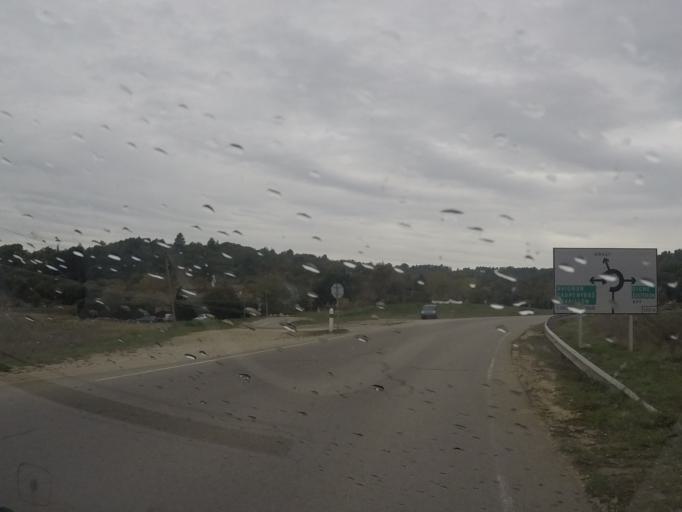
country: FR
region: Provence-Alpes-Cote d'Azur
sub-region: Departement du Vaucluse
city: Goult
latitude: 43.8577
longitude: 5.2670
